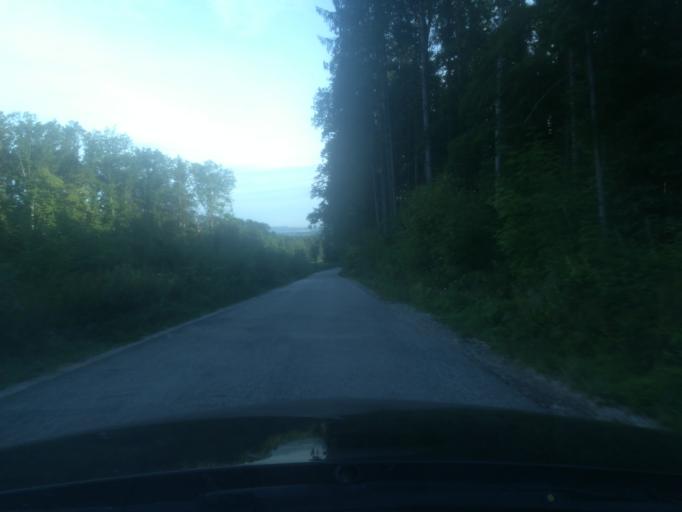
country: AT
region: Upper Austria
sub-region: Wels-Land
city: Marchtrenk
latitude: 48.1691
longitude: 14.1655
